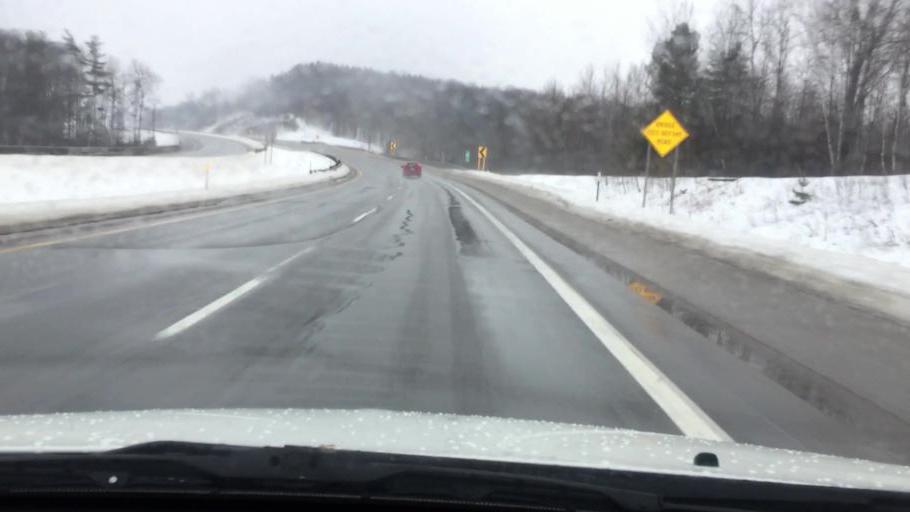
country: US
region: Michigan
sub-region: Wexford County
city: Cadillac
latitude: 44.3014
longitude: -85.3926
